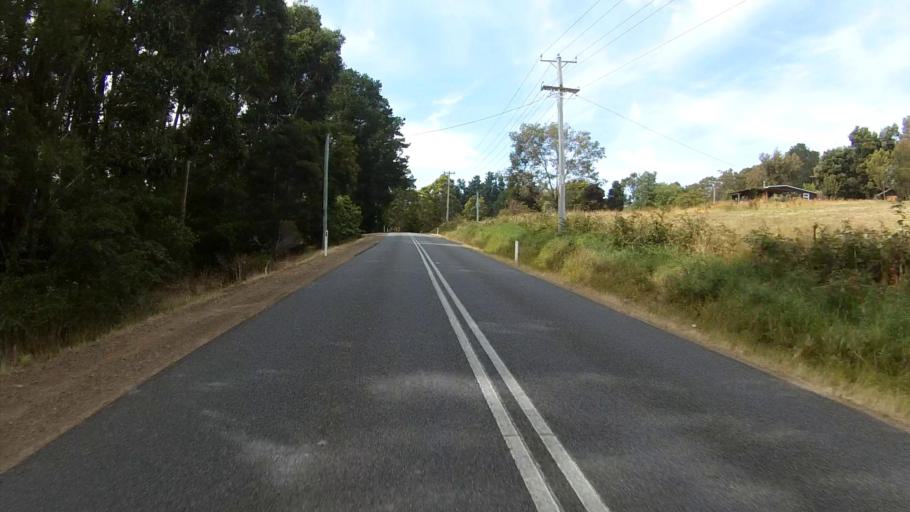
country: AU
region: Tasmania
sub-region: Kingborough
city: Kettering
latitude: -43.1838
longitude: 147.2410
